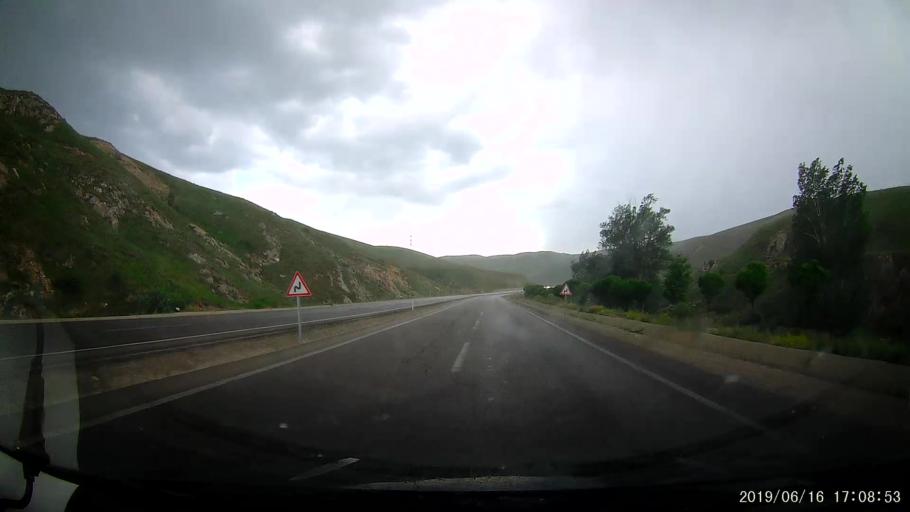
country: TR
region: Erzurum
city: Askale
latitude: 39.9021
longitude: 40.6568
